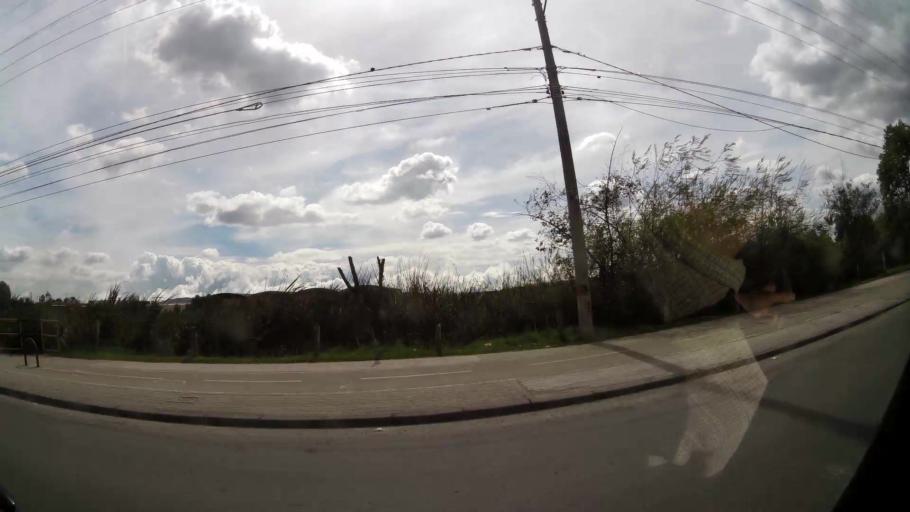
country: CO
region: Cundinamarca
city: Funza
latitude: 4.7018
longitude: -74.2016
